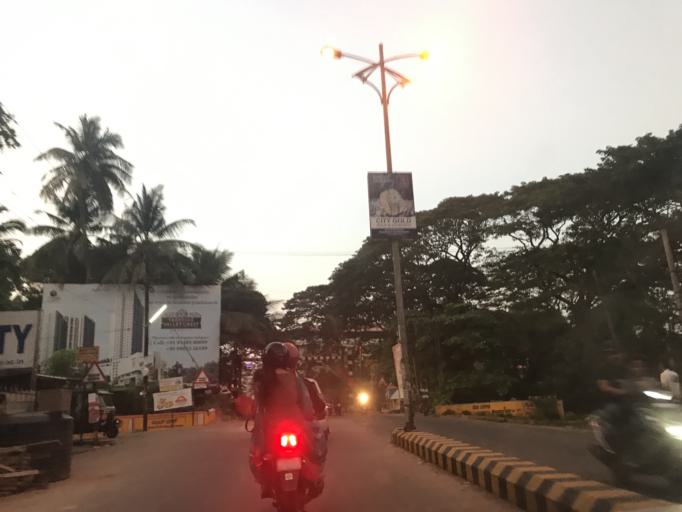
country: IN
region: Karnataka
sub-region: Dakshina Kannada
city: Ullal
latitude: 12.8531
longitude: 74.8410
